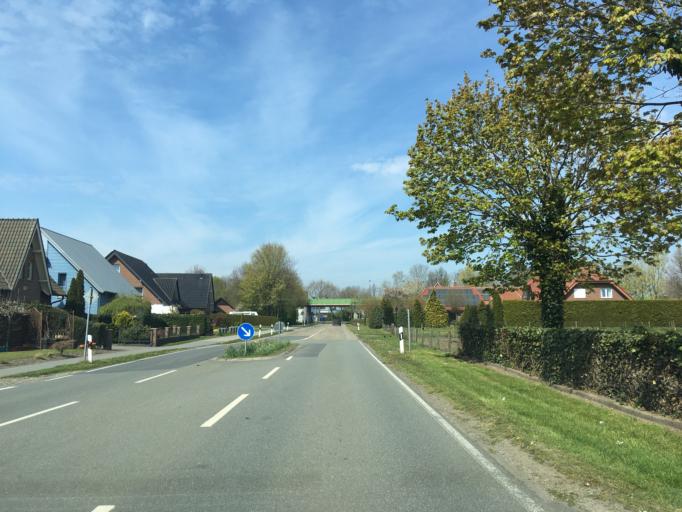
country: DE
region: North Rhine-Westphalia
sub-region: Regierungsbezirk Munster
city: Vreden
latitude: 52.0230
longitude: 6.8315
